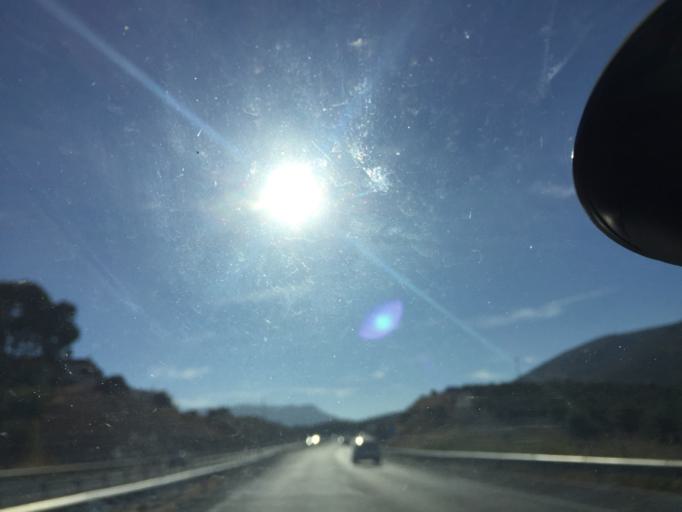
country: ES
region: Andalusia
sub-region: Provincia de Jaen
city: La Guardia de Jaen
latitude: 37.7686
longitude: -3.7256
